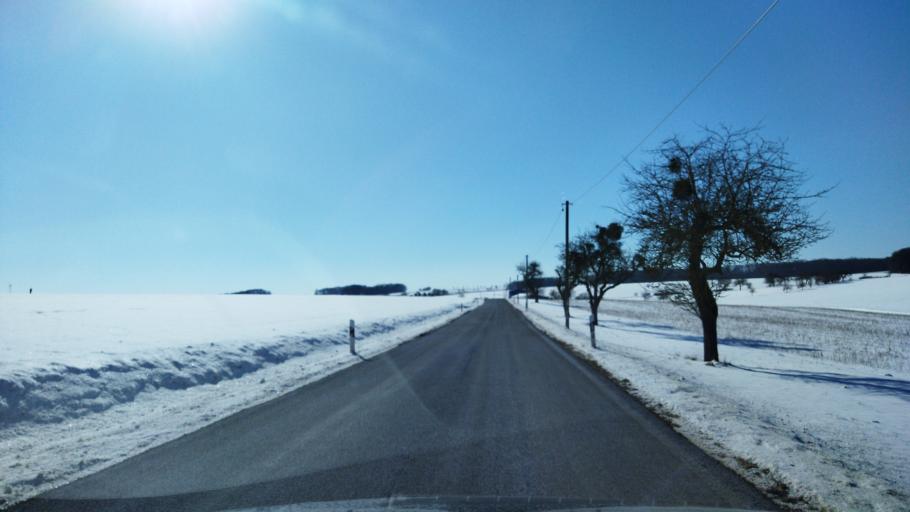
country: DE
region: Baden-Wuerttemberg
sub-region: Regierungsbezirk Stuttgart
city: Langenburg
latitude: 49.2563
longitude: 9.8960
